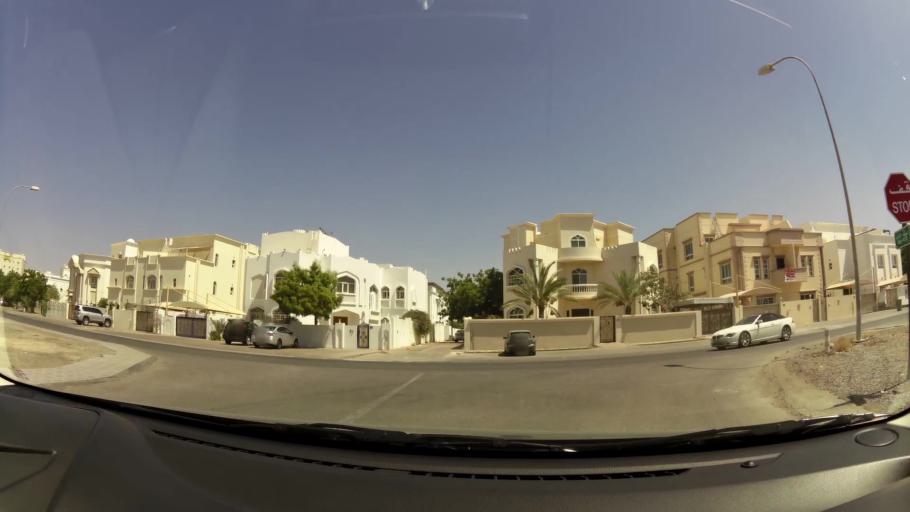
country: OM
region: Muhafazat Masqat
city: Bawshar
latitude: 23.5967
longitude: 58.3664
